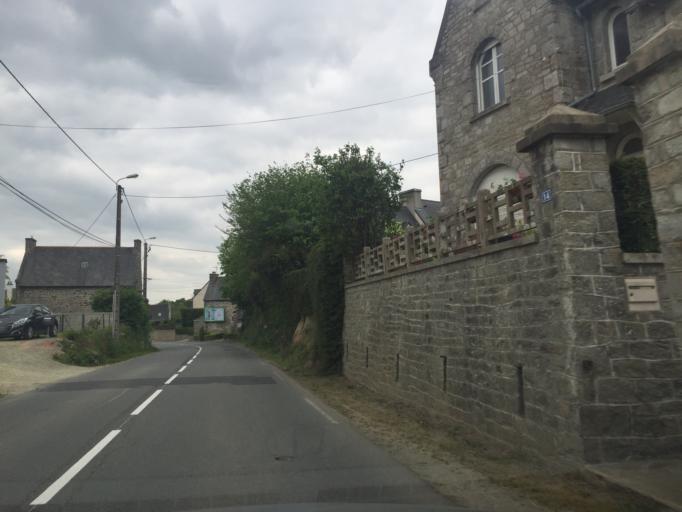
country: FR
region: Brittany
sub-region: Departement des Cotes-d'Armor
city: Saint-Cast-le-Guildo
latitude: 48.6098
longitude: -2.2550
